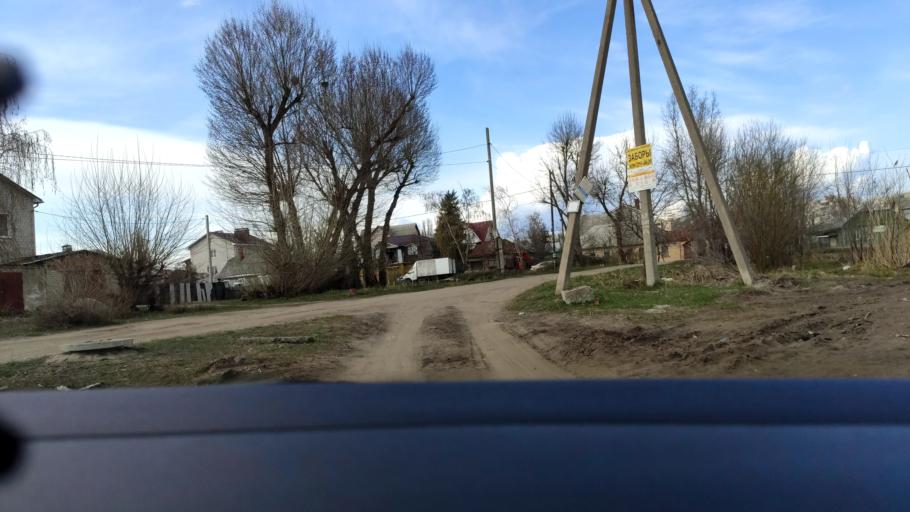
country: RU
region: Voronezj
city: Maslovka
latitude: 51.6285
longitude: 39.2777
